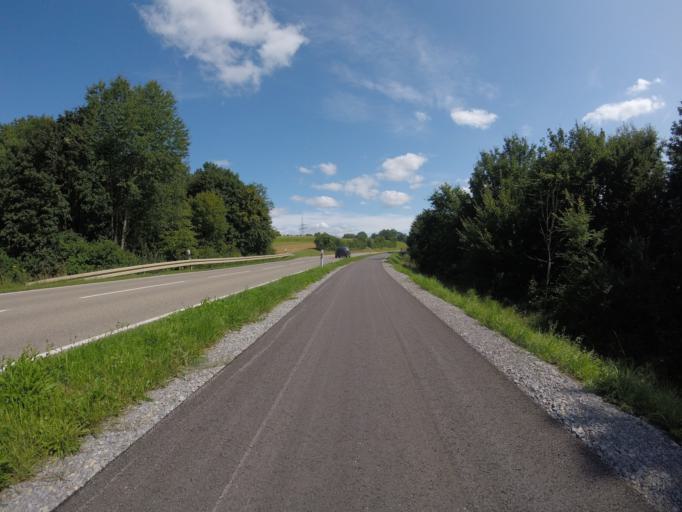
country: DE
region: Baden-Wuerttemberg
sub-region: Regierungsbezirk Stuttgart
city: Oppenweiler
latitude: 48.9650
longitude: 9.4666
